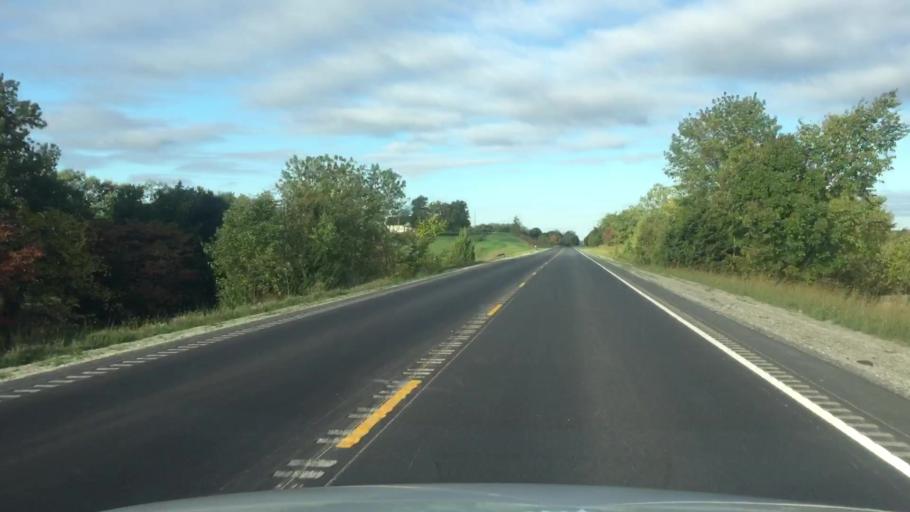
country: US
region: Missouri
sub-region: Boone County
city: Columbia
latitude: 38.9892
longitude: -92.4987
